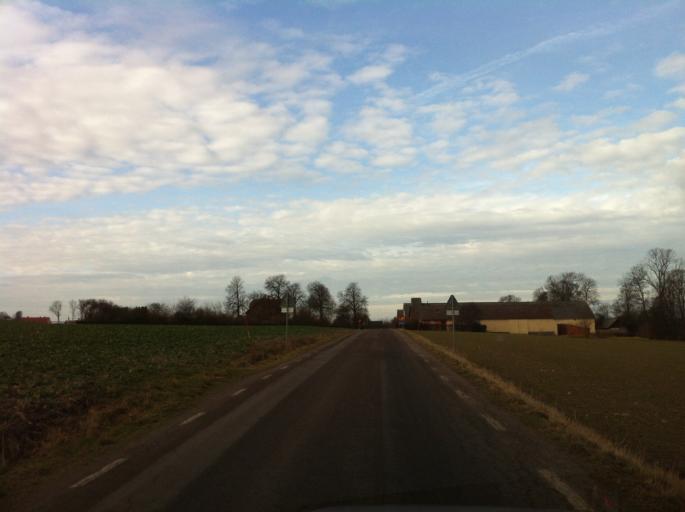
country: SE
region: Skane
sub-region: Landskrona
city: Asmundtorp
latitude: 55.9229
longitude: 12.9661
